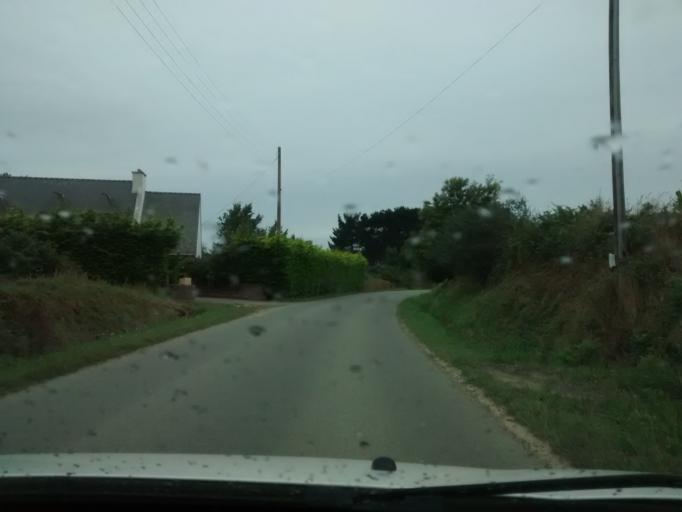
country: FR
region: Brittany
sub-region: Departement des Cotes-d'Armor
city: Penvenan
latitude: 48.8205
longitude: -3.3051
